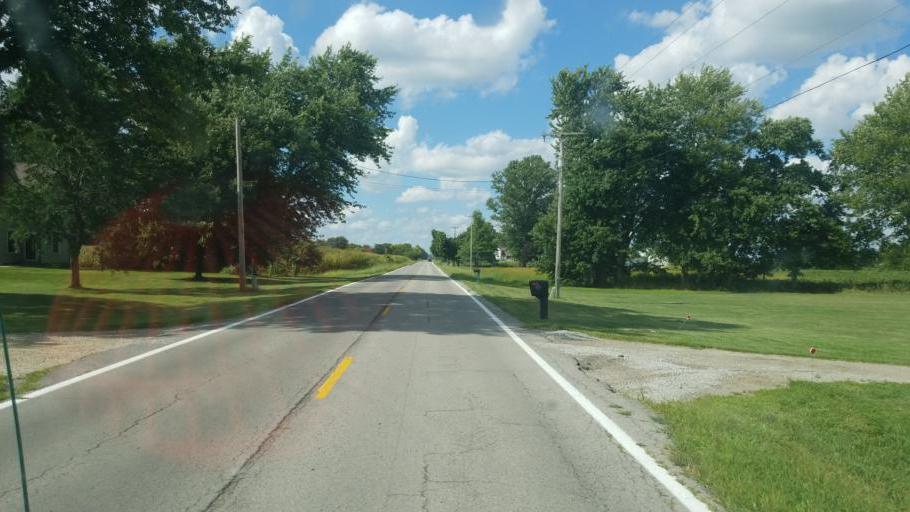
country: US
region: Ohio
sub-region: Union County
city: Richwood
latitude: 40.4019
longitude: -83.2842
